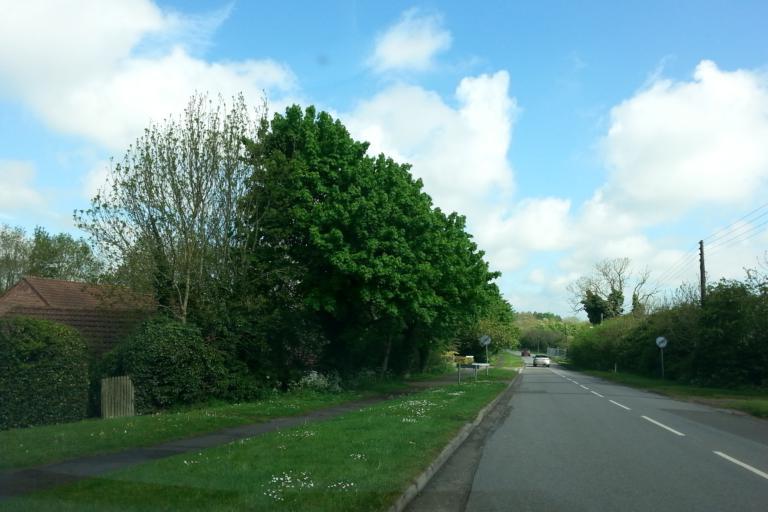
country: GB
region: England
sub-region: District of Rutland
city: Greetham
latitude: 52.8084
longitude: -0.6207
